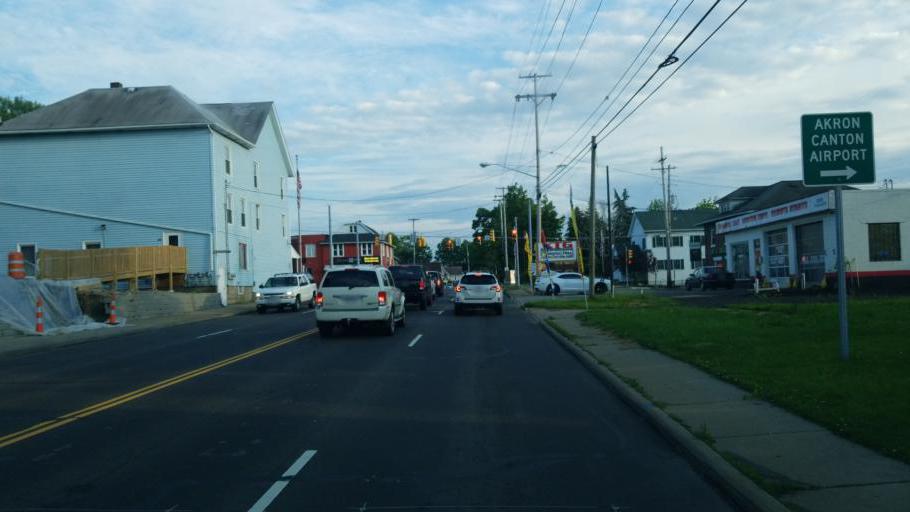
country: US
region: Ohio
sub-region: Stark County
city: Greentown
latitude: 40.9282
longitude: -81.4028
